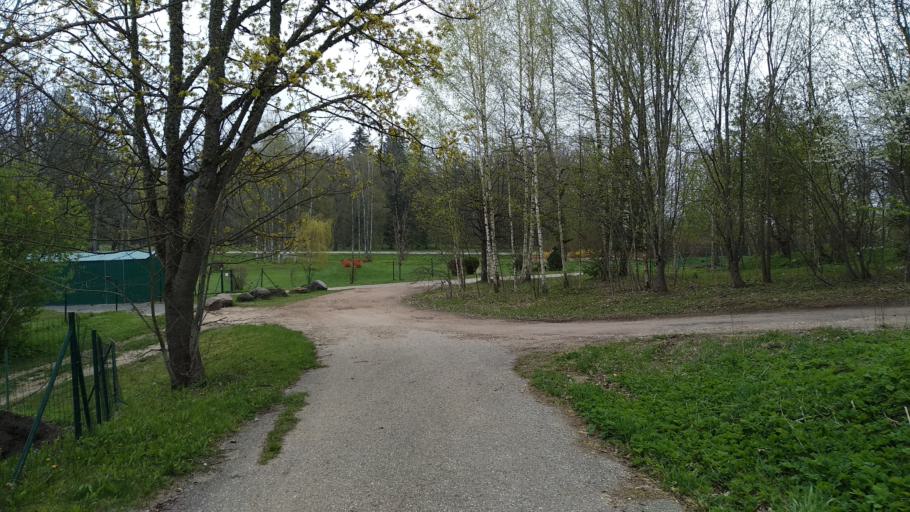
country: LV
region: Malpils
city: Malpils
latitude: 57.0084
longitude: 24.9475
